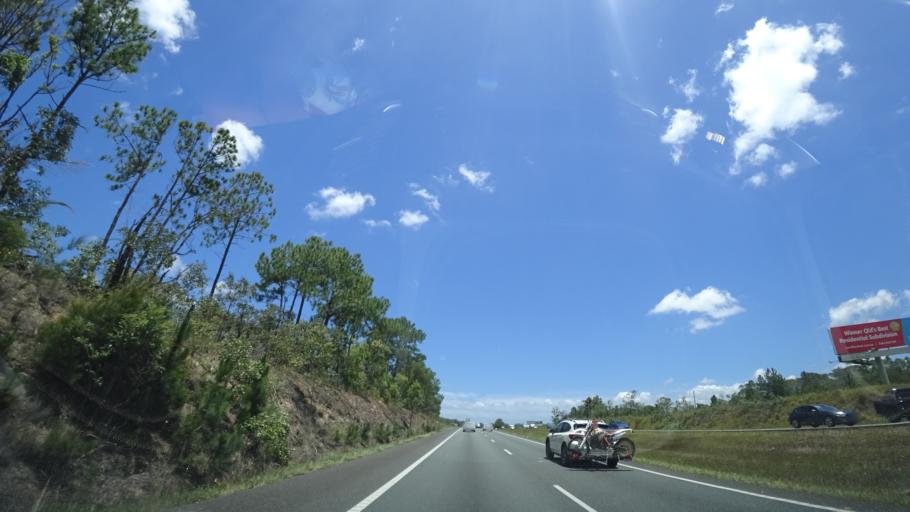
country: AU
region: Queensland
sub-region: Moreton Bay
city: Caboolture
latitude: -27.0180
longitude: 152.9773
